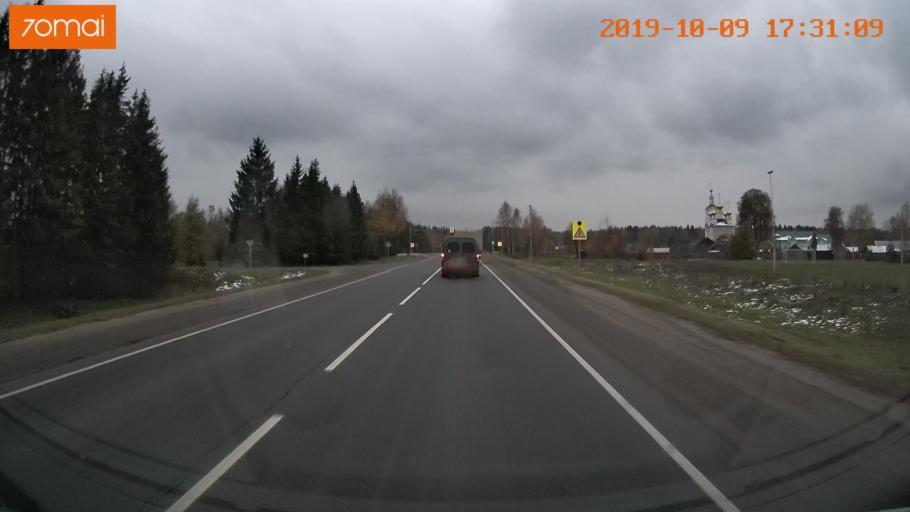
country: RU
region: Ivanovo
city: Bogorodskoye
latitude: 57.1375
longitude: 41.0422
